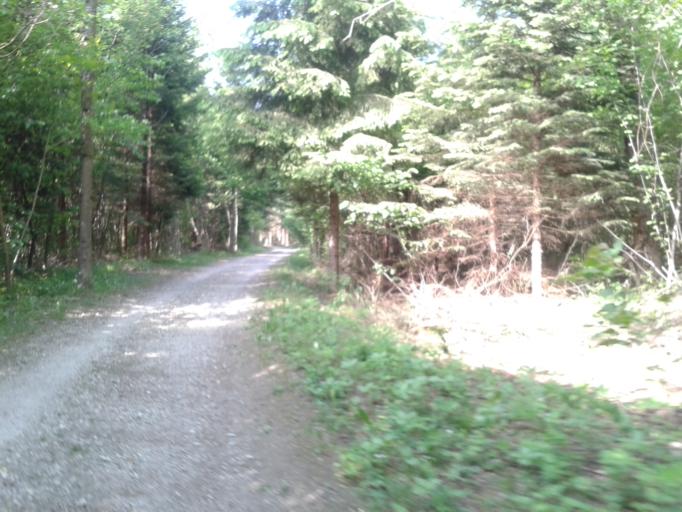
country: IT
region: Trentino-Alto Adige
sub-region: Provincia di Trento
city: Storo
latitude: 45.8653
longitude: 10.5823
